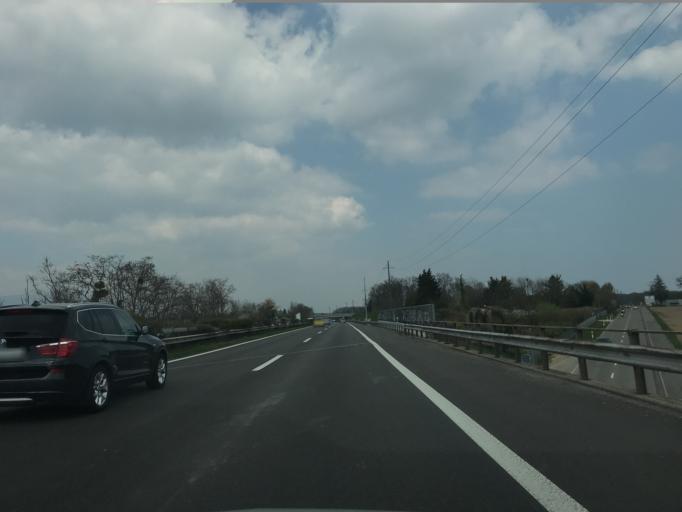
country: CH
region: Geneva
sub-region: Geneva
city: Bellevue
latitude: 46.2700
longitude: 6.1375
